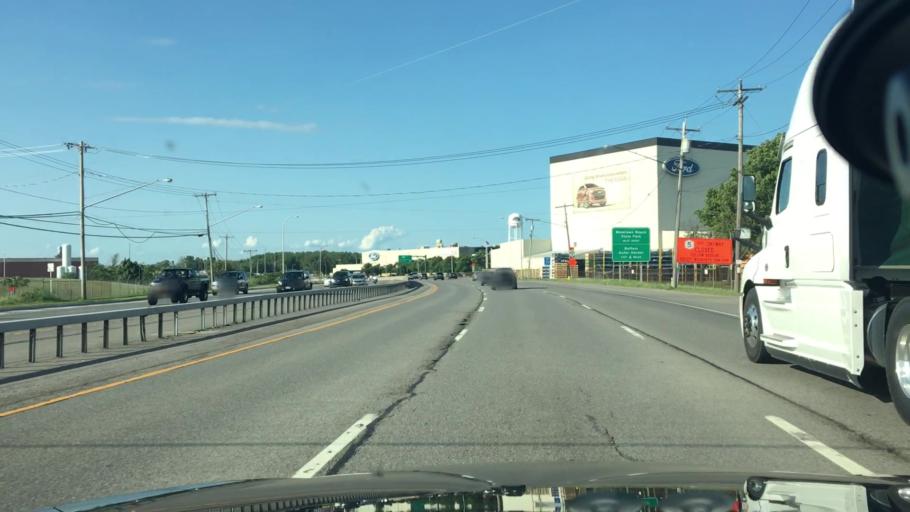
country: US
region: New York
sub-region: Erie County
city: Blasdell
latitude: 42.7837
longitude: -78.8491
